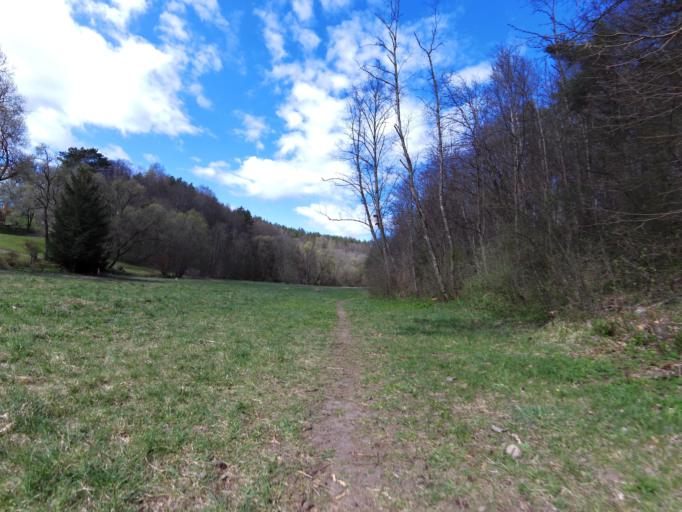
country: LT
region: Vilnius County
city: Pilaite
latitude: 54.6943
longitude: 25.1897
